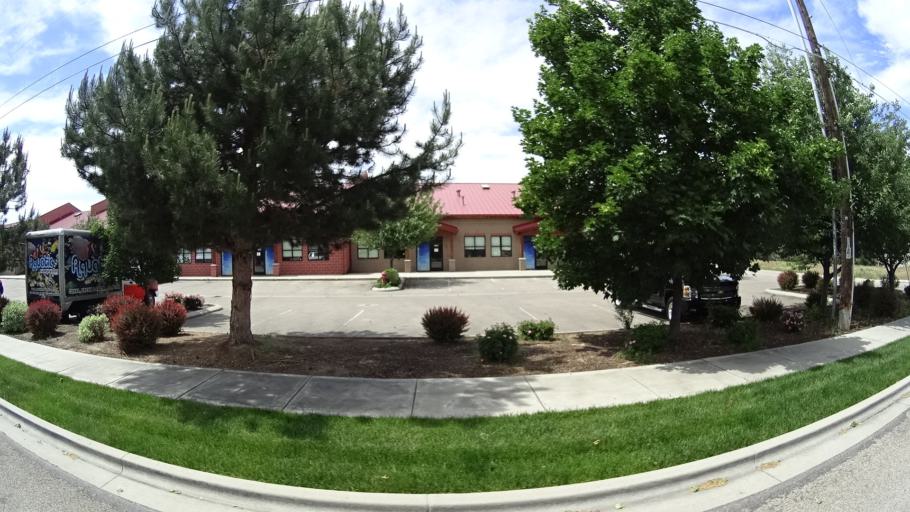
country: US
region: Idaho
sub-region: Ada County
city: Meridian
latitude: 43.6232
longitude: -116.3204
